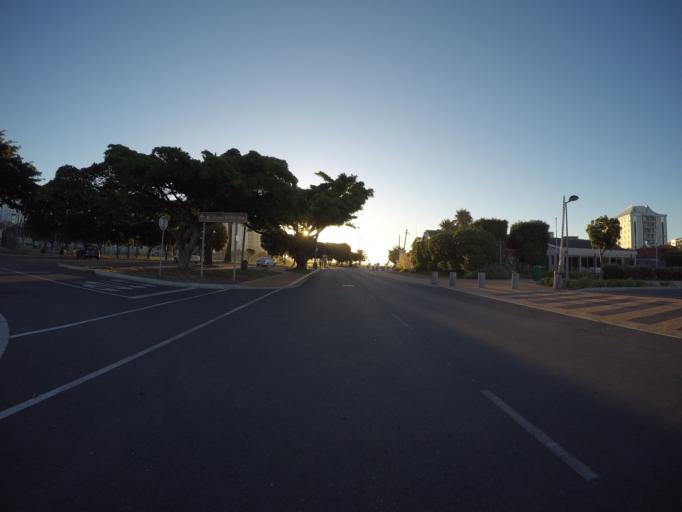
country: ZA
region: Western Cape
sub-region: City of Cape Town
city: Cape Town
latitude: -33.9058
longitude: 18.4009
